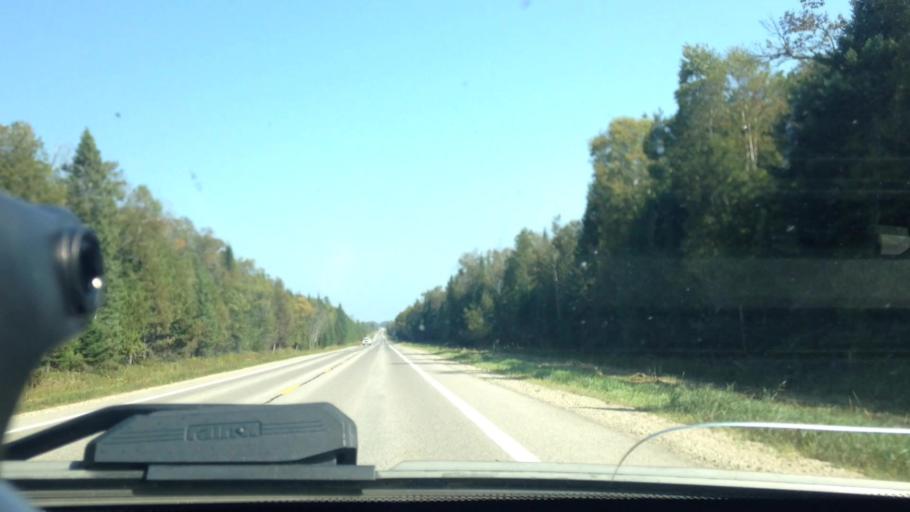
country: US
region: Michigan
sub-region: Luce County
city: Newberry
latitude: 46.3036
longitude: -85.4143
